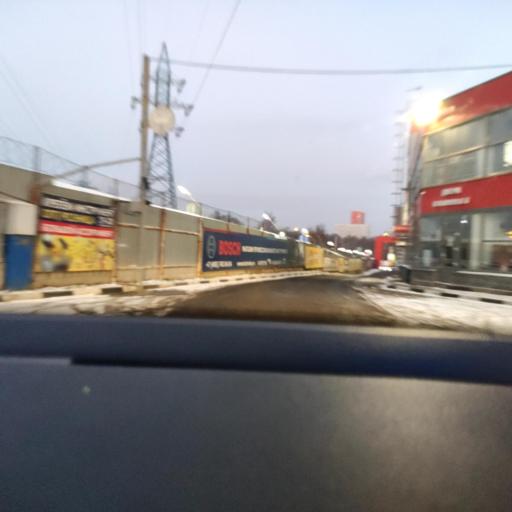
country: RU
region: Moskovskaya
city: Reutov
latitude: 55.7774
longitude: 37.8535
